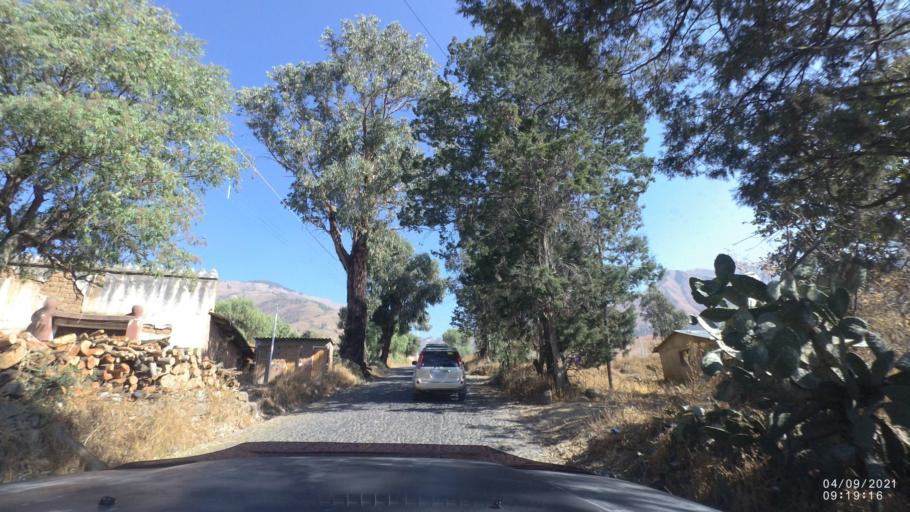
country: BO
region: Cochabamba
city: Sipe Sipe
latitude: -17.3676
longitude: -66.3582
